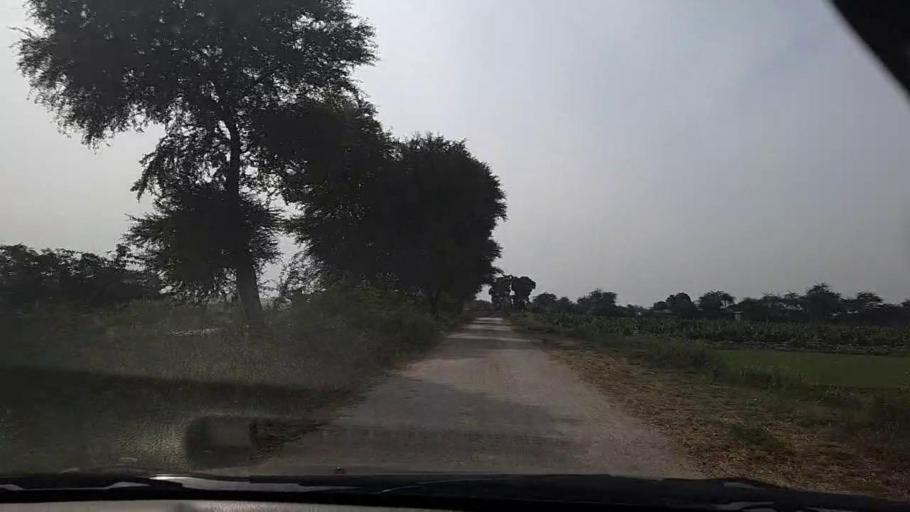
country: PK
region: Sindh
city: Thatta
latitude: 24.5754
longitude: 67.8796
